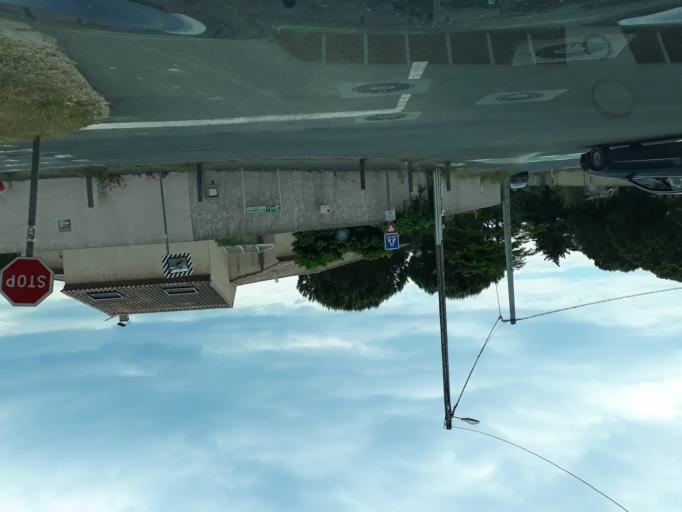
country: FR
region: Languedoc-Roussillon
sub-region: Departement de l'Herault
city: Agde
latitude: 43.2911
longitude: 3.4635
